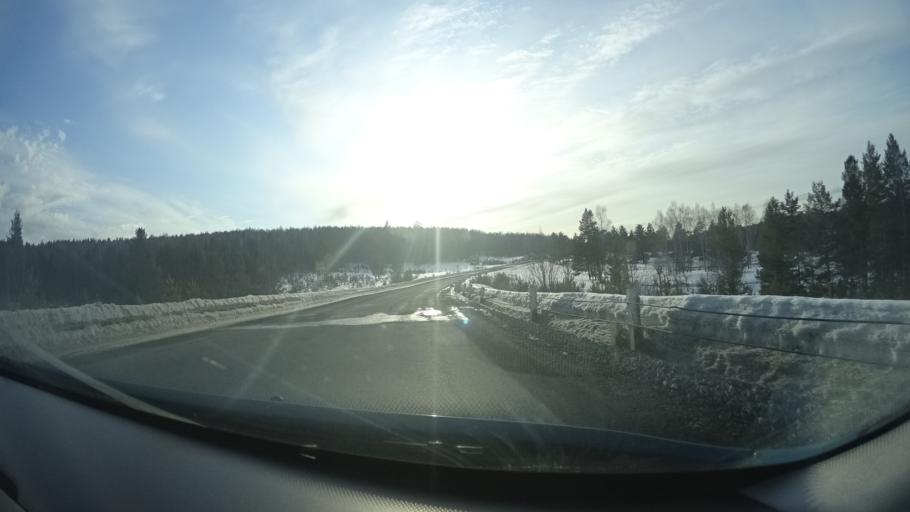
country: RU
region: Bashkortostan
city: Lomovka
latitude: 53.6724
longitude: 58.2406
